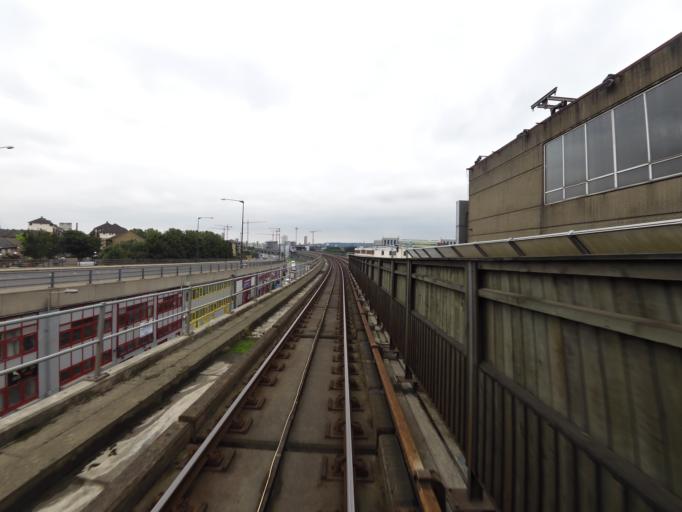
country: GB
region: England
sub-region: Greater London
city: Poplar
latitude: 51.5049
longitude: 0.0173
